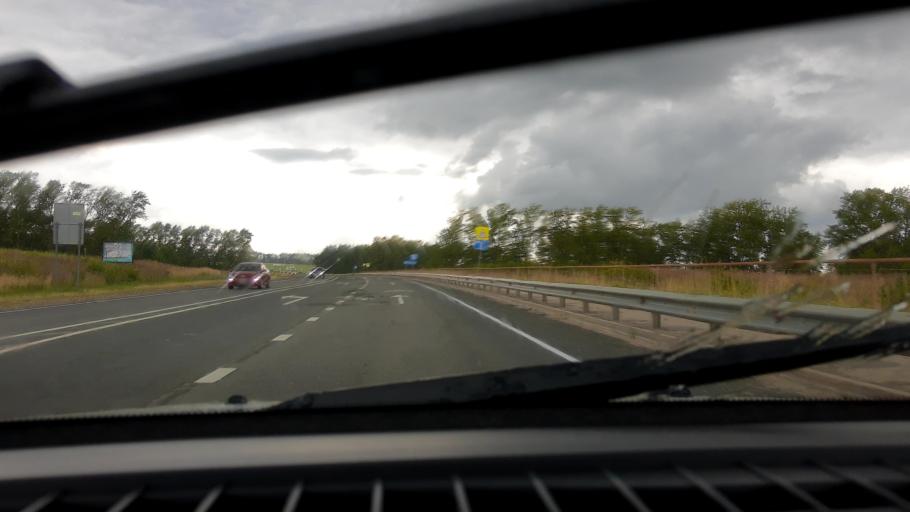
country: RU
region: Nizjnij Novgorod
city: Bol'shoye Murashkino
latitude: 55.8857
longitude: 44.7471
